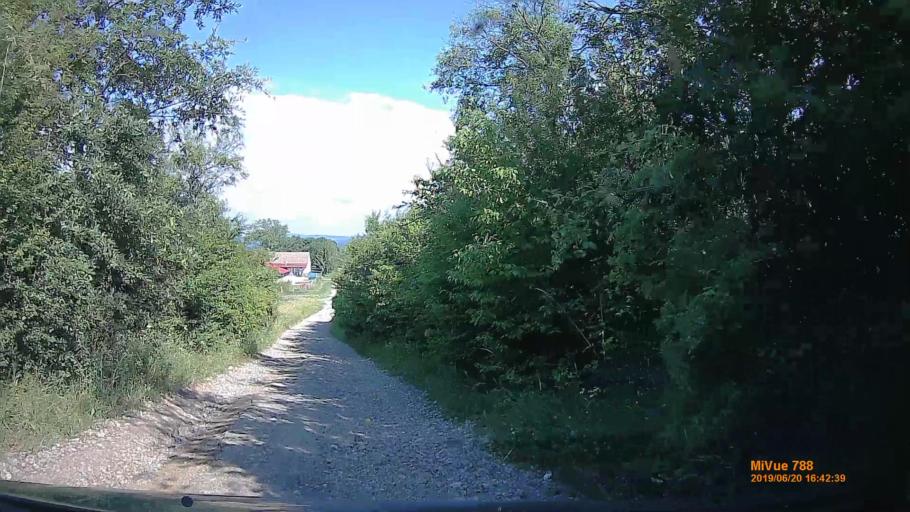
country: HU
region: Baranya
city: Buekkoesd
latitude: 46.1610
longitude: 18.0361
